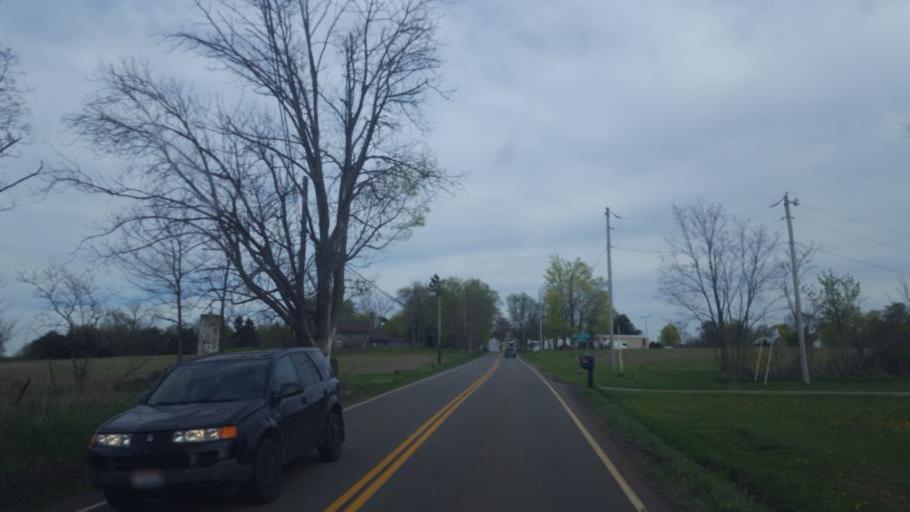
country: US
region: Ohio
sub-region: Crawford County
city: Galion
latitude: 40.7095
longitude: -82.7201
